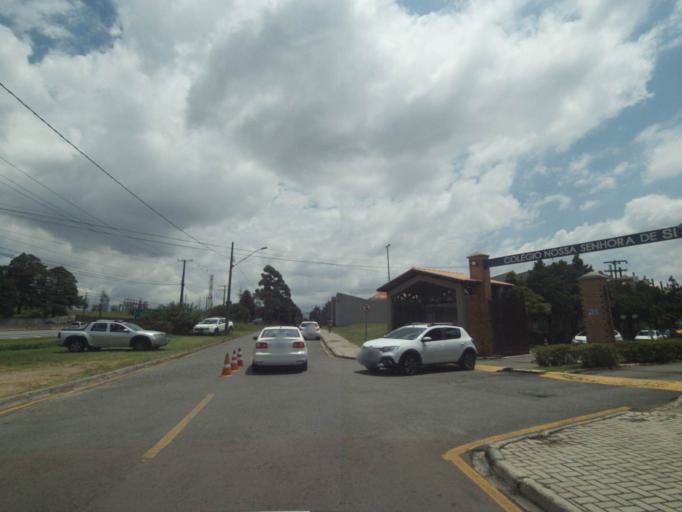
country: BR
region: Parana
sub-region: Pinhais
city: Pinhais
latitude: -25.4769
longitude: -49.2048
